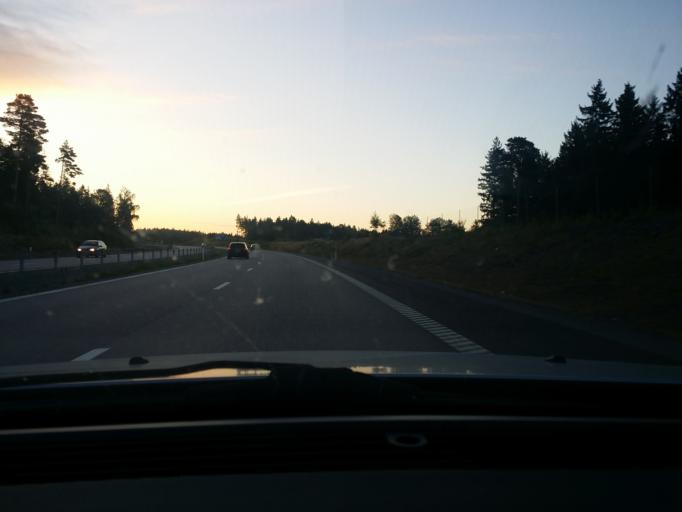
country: SE
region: Uppsala
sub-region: Enkopings Kommun
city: Enkoping
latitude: 59.6436
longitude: 17.0412
